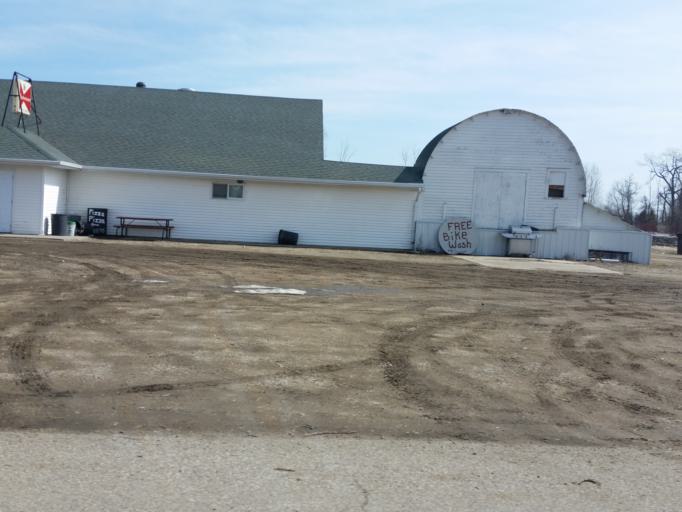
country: US
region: North Dakota
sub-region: Walsh County
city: Grafton
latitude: 48.2971
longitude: -97.2548
